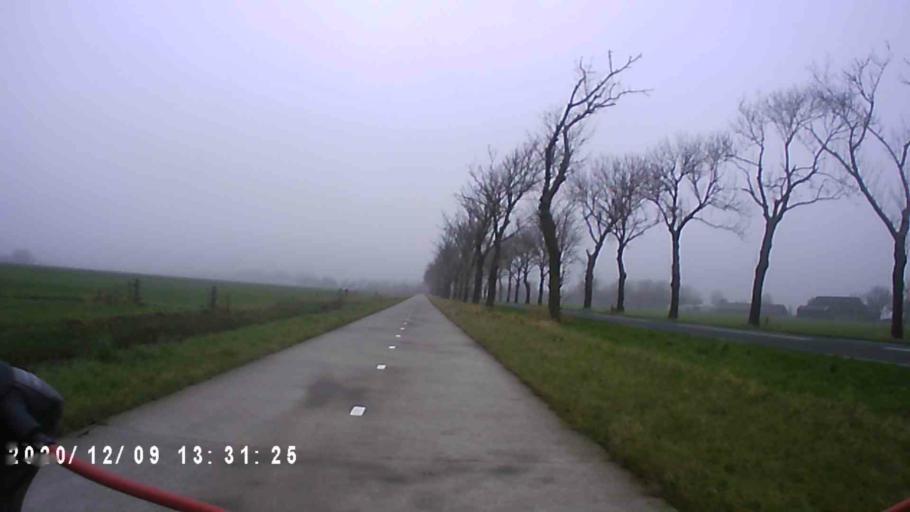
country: NL
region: Groningen
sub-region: Gemeente Bedum
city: Bedum
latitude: 53.2737
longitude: 6.5978
